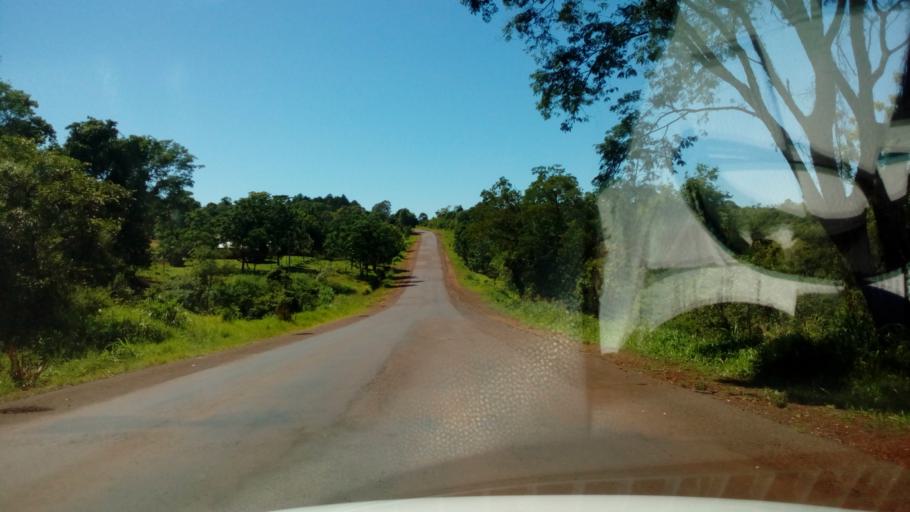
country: AR
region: Misiones
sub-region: Departamento de Leandro N. Alem
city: Leandro N. Alem
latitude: -27.5931
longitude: -55.3559
